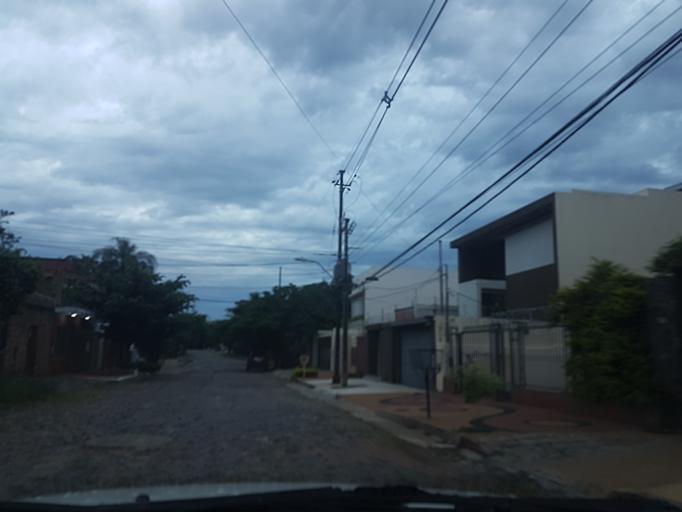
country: PY
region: Asuncion
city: Asuncion
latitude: -25.2778
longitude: -57.5965
